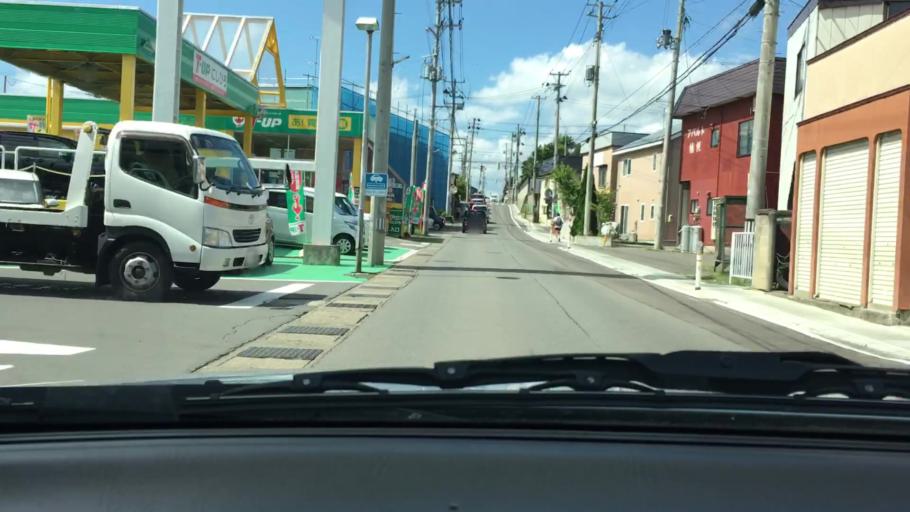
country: JP
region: Aomori
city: Hirosaki
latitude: 40.5862
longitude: 140.4652
